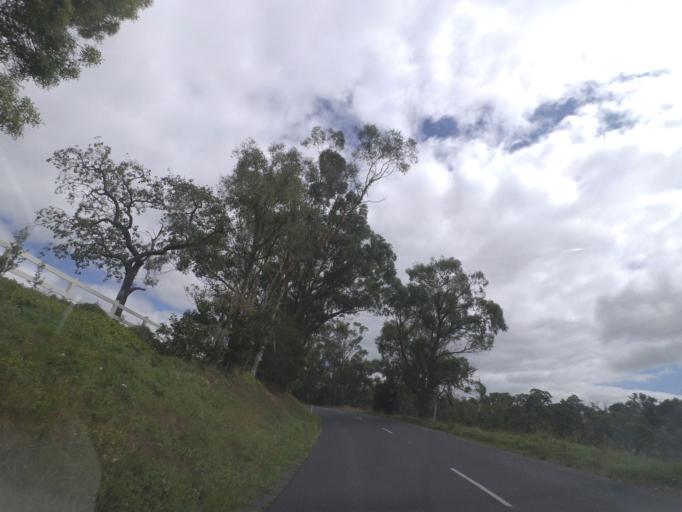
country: AU
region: Victoria
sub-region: Yarra Ranges
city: Woori Yallock
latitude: -37.8091
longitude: 145.5031
